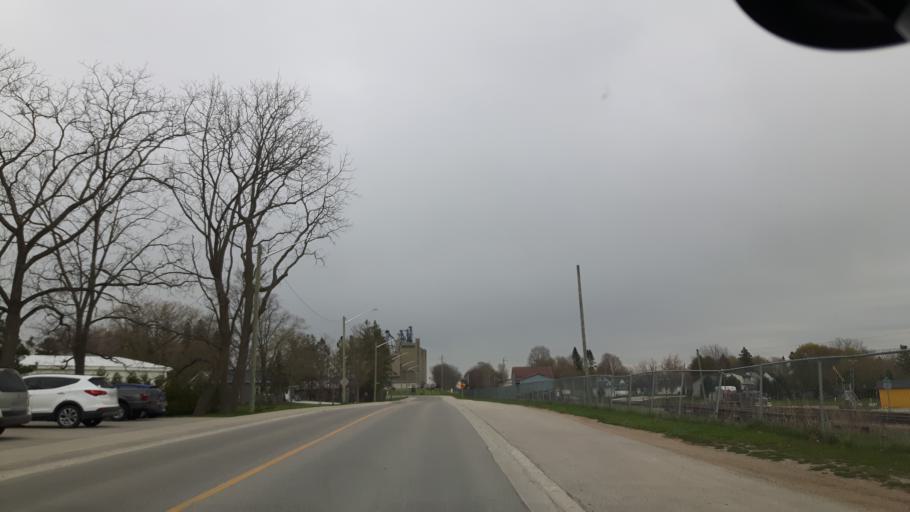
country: CA
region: Ontario
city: Bluewater
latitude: 43.6116
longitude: -81.5393
